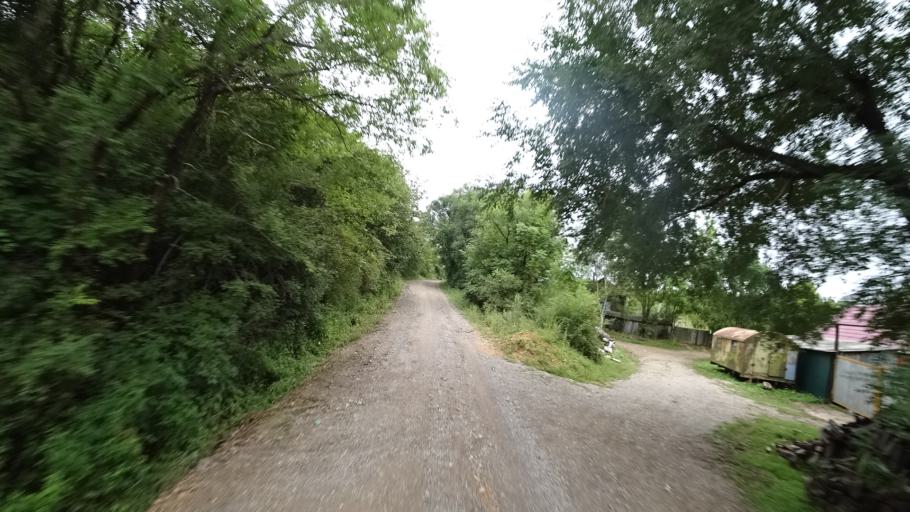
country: RU
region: Primorskiy
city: Rettikhovka
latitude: 44.1633
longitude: 132.7458
